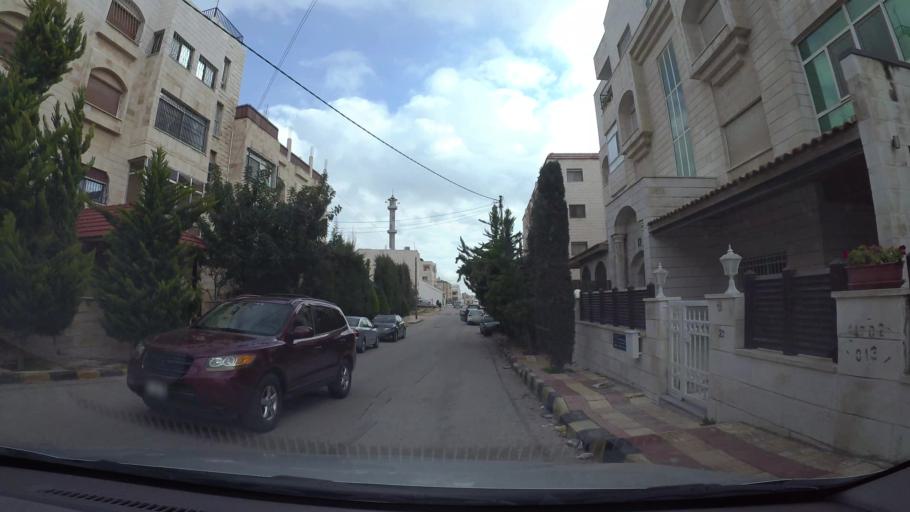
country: JO
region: Amman
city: Wadi as Sir
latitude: 31.9850
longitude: 35.8461
